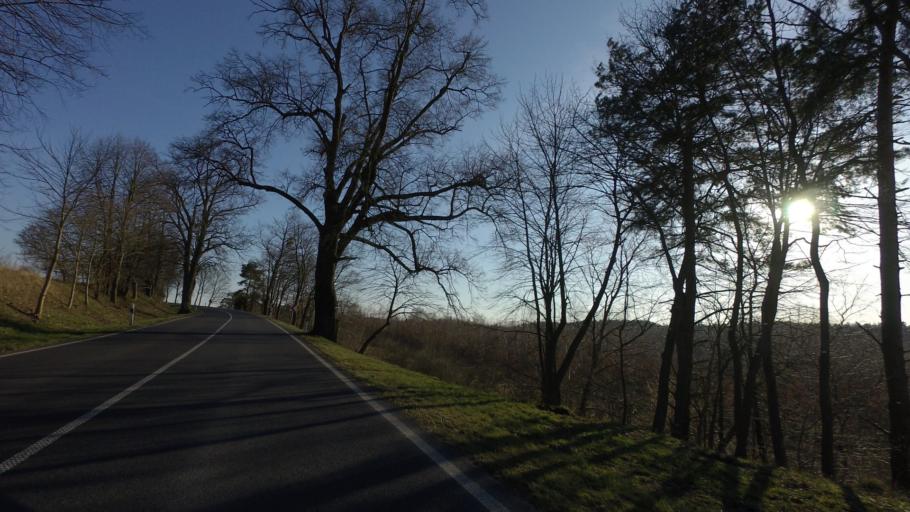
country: DE
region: Brandenburg
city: Althuttendorf
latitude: 52.9316
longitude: 13.7913
